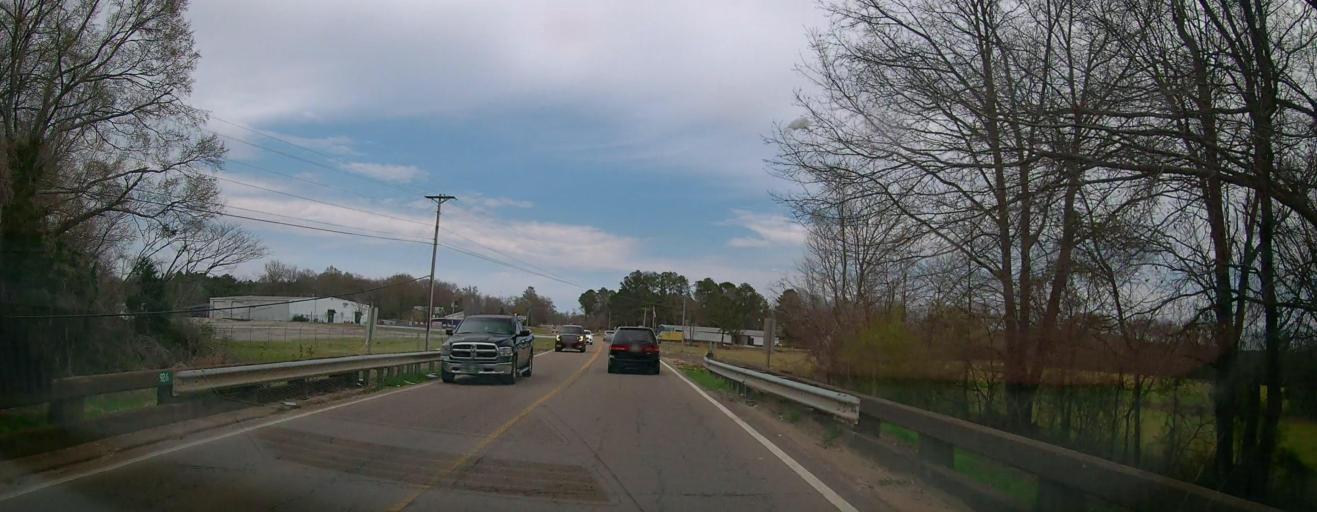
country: US
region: Mississippi
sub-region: Lee County
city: Plantersville
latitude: 34.2597
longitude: -88.6491
